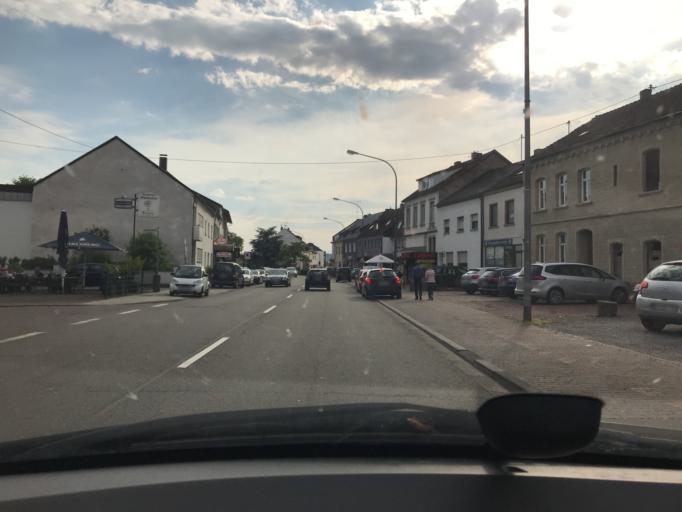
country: DE
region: Saarland
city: Saarlouis
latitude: 49.3269
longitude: 6.7673
